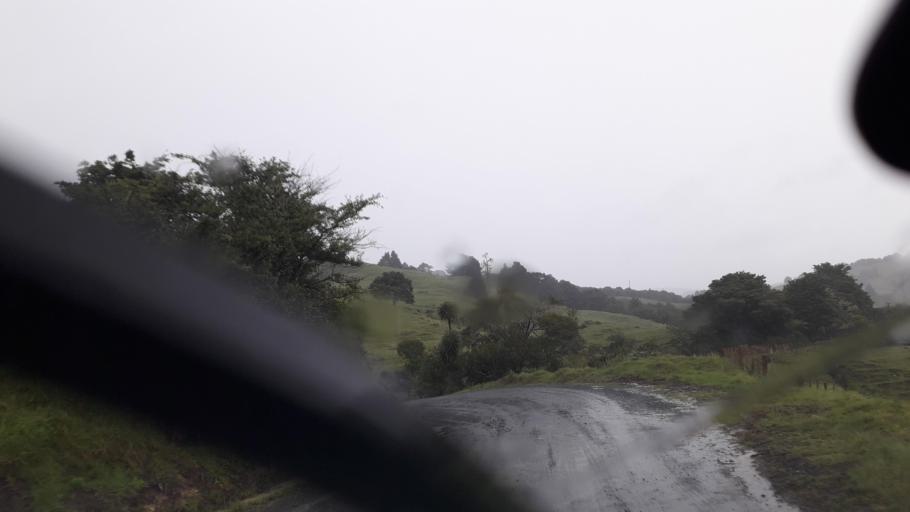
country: NZ
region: Northland
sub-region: Far North District
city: Kerikeri
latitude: -35.1317
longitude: 173.7263
